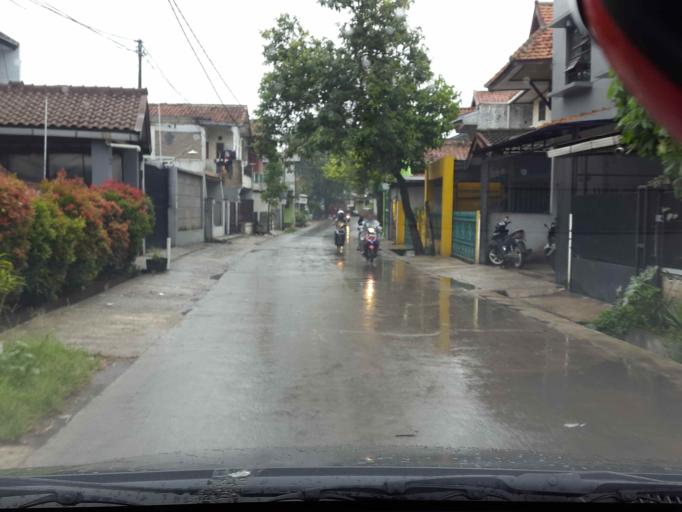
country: ID
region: West Java
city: Cimahi
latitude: -6.8881
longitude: 107.5657
